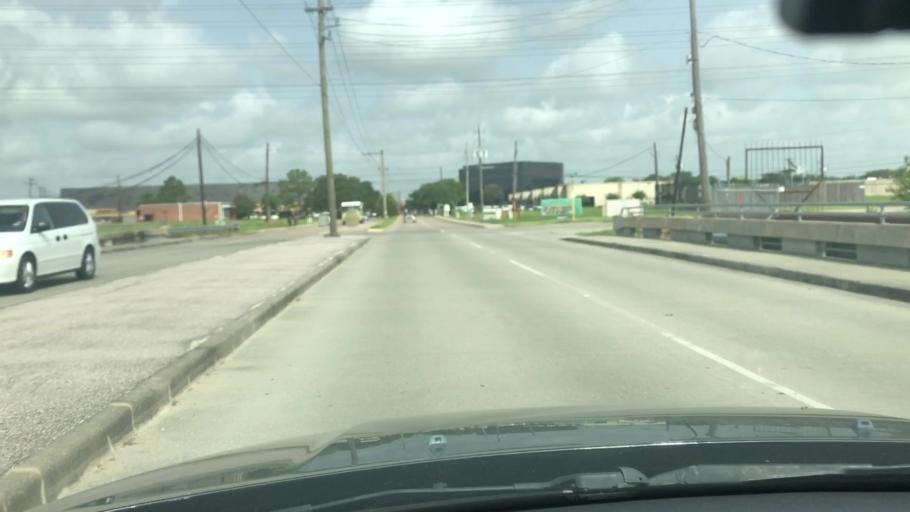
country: US
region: Texas
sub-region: Harris County
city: Webster
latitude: 29.5504
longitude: -95.1116
